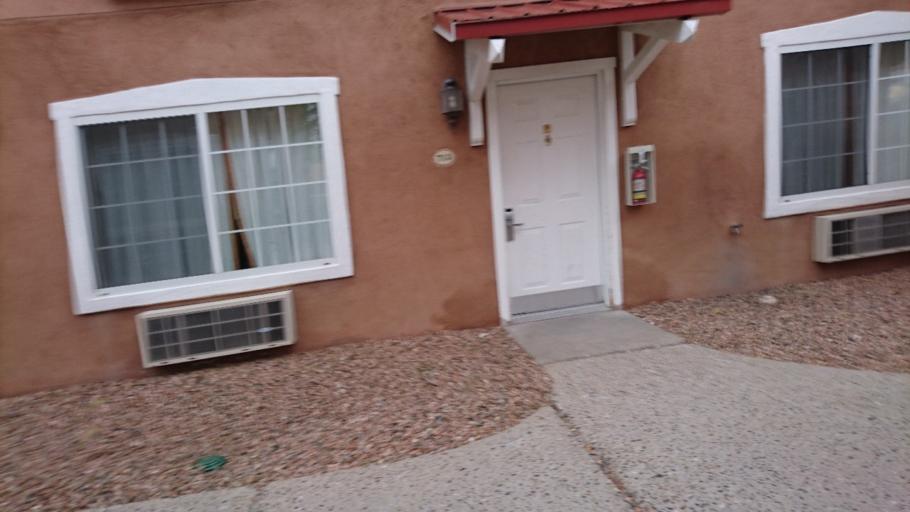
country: US
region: New Mexico
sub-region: Santa Fe County
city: Santa Fe
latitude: 35.6446
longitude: -105.9543
